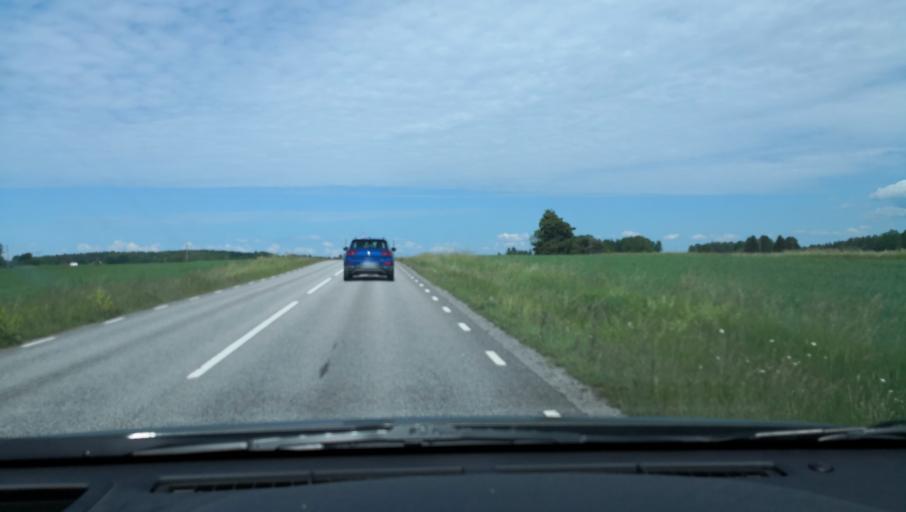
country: SE
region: Stockholm
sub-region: Sigtuna Kommun
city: Sigtuna
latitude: 59.6663
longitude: 17.6923
